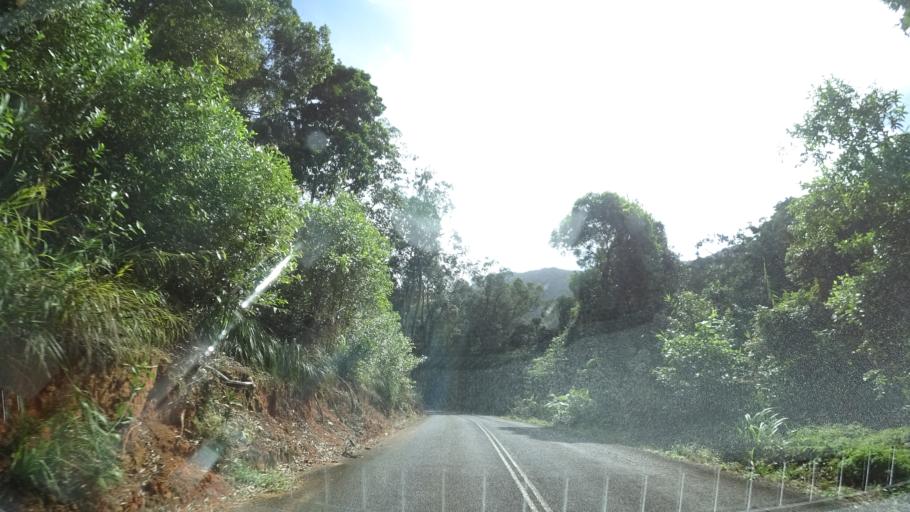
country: AU
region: Queensland
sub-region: Cairns
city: Port Douglas
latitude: -16.2580
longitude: 145.4205
